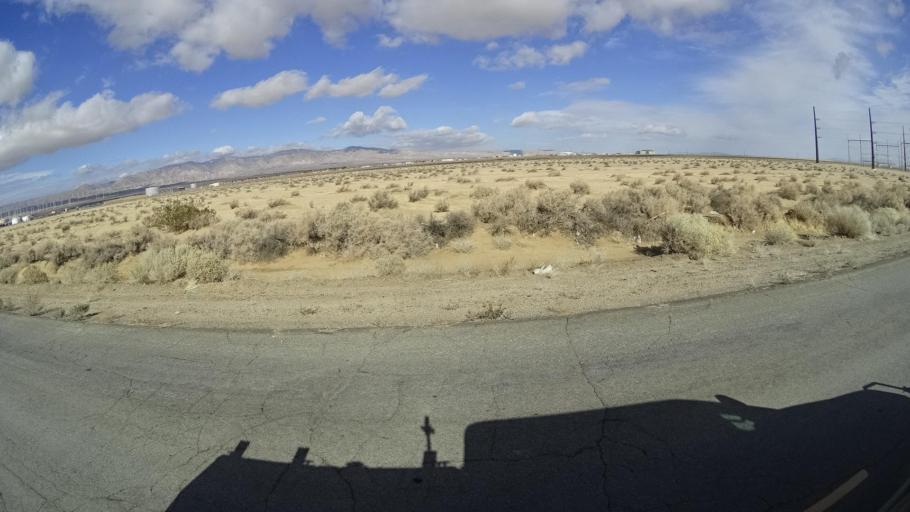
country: US
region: California
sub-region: Kern County
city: Mojave
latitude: 35.0250
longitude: -118.1541
